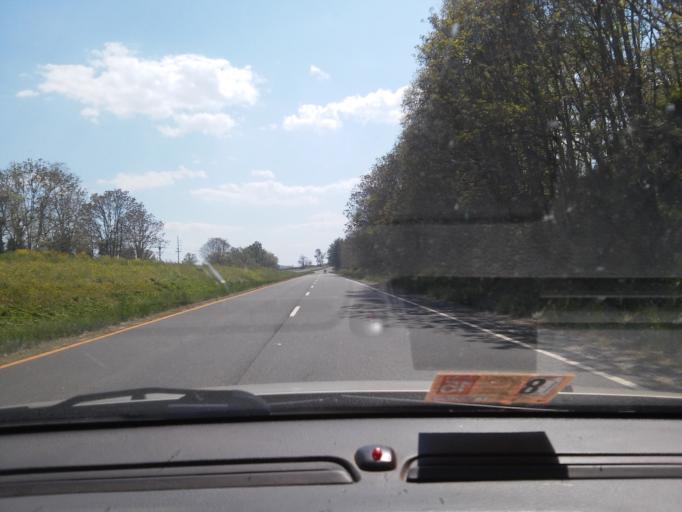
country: US
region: Virginia
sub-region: Rappahannock County
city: Washington
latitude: 38.7022
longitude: -78.1607
